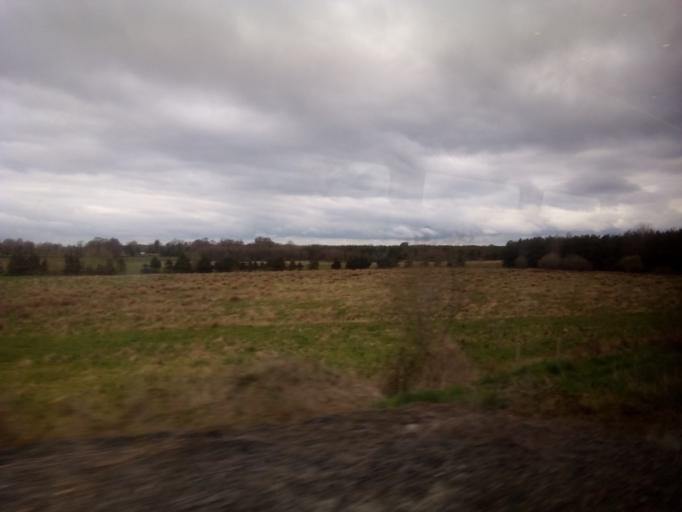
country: IE
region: Leinster
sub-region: An Longfort
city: Edgeworthstown
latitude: 53.6818
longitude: -7.5643
